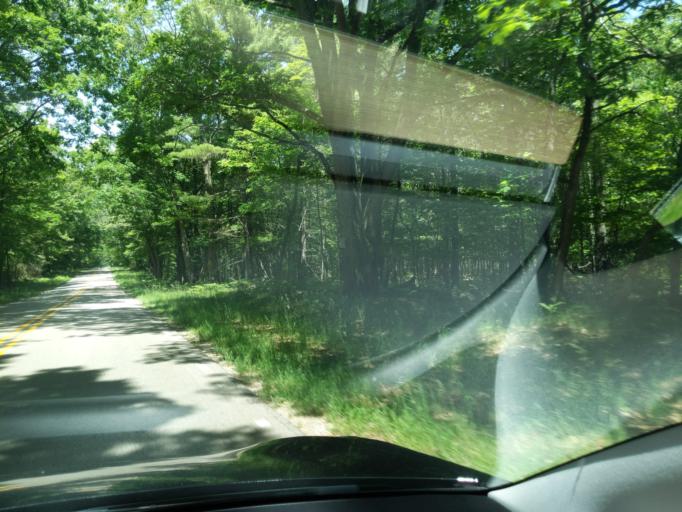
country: US
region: Michigan
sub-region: Muskegon County
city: Montague
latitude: 43.3911
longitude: -86.4162
